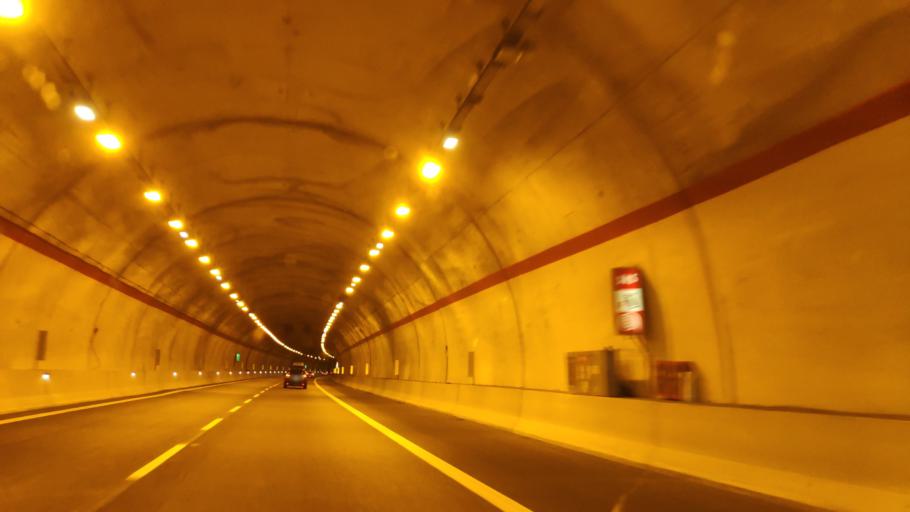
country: IT
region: Calabria
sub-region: Provincia di Cosenza
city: Mormanno
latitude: 39.8809
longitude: 15.9857
